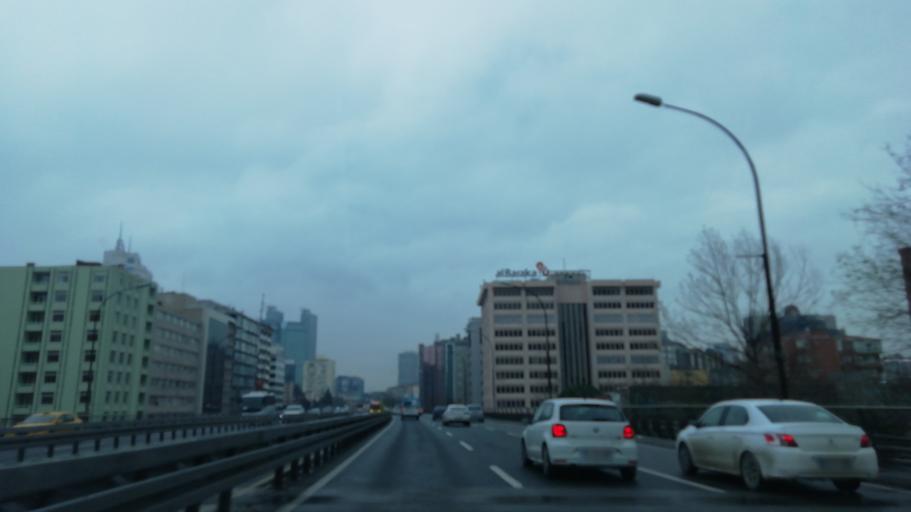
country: TR
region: Istanbul
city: Sisli
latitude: 41.0665
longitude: 28.9998
